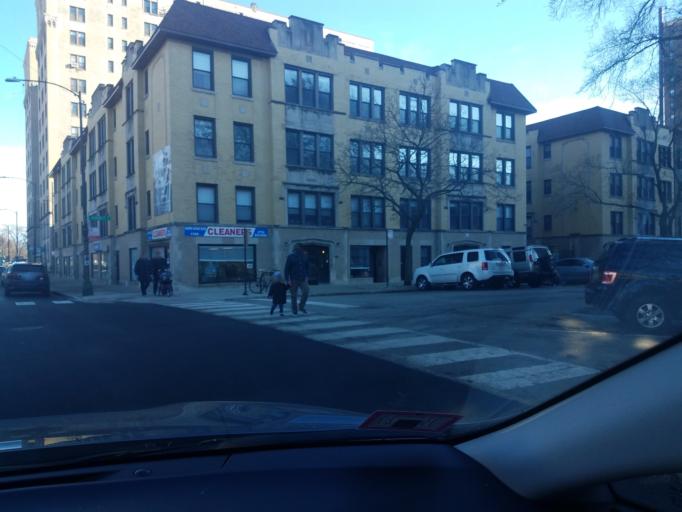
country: US
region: Illinois
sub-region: Cook County
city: Chicago
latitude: 41.7952
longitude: -87.5827
